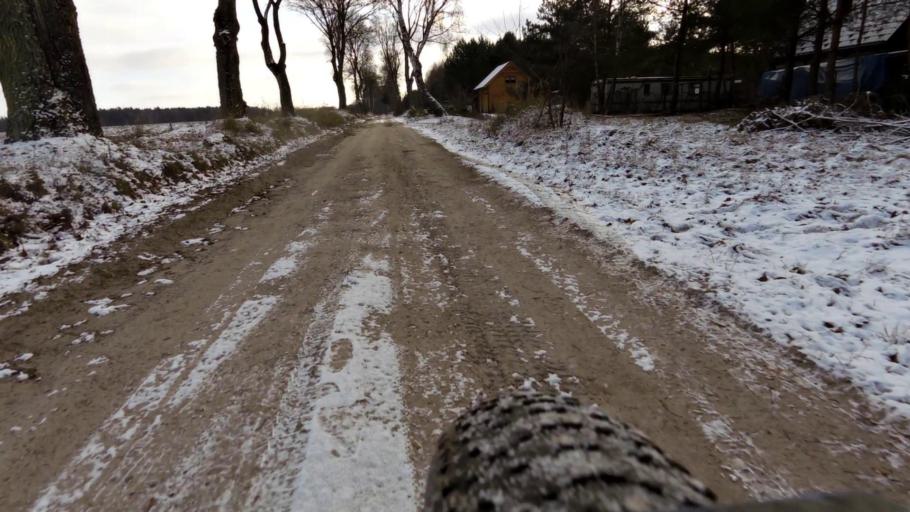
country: PL
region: West Pomeranian Voivodeship
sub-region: Powiat walecki
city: Walcz
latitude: 53.2700
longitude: 16.3095
